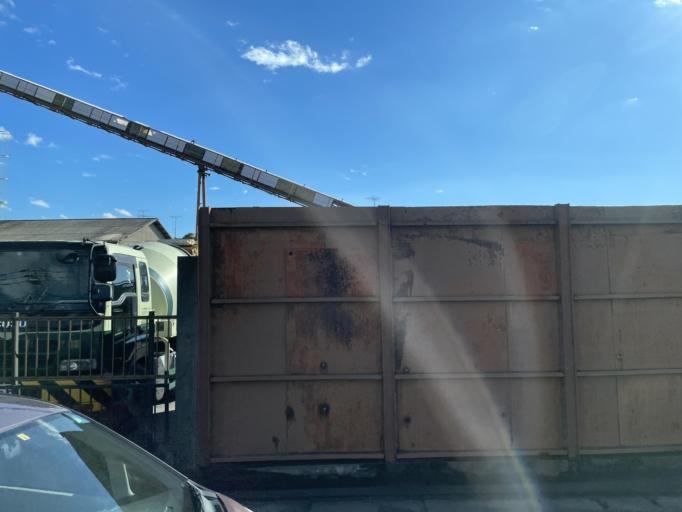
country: JP
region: Chiba
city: Noda
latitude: 35.9323
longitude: 139.8225
